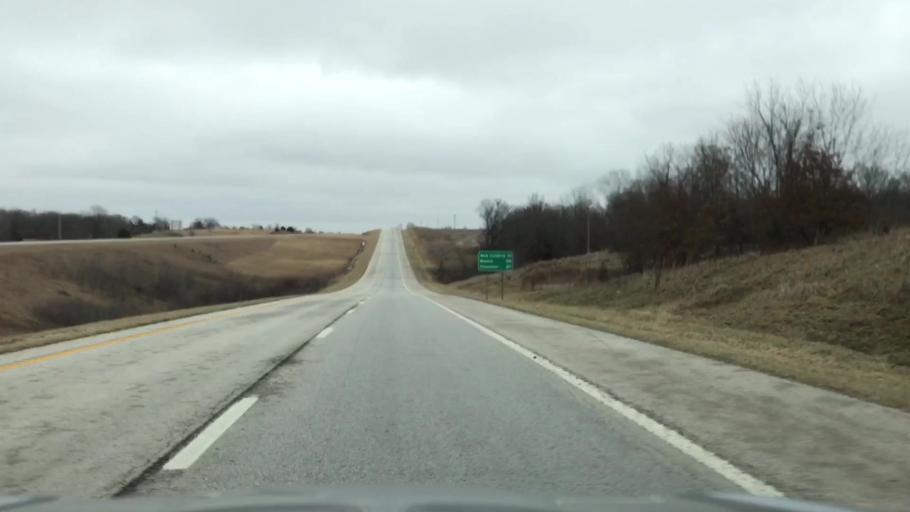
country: US
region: Missouri
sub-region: Linn County
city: Marceline
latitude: 39.7602
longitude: -92.9254
